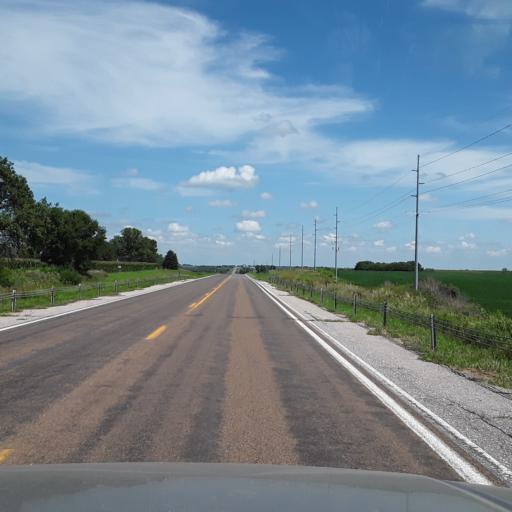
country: US
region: Nebraska
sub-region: York County
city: York
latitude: 40.9619
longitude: -97.4061
